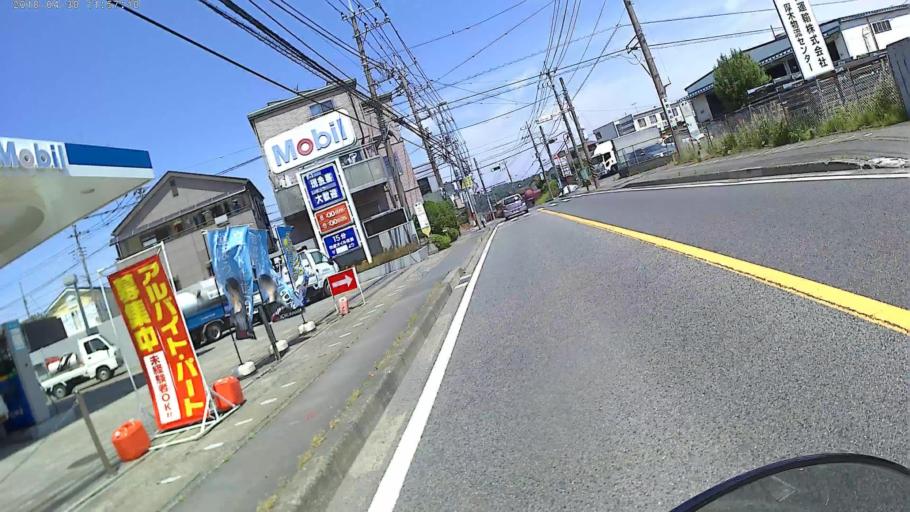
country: JP
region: Kanagawa
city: Zama
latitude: 35.4949
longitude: 139.3401
